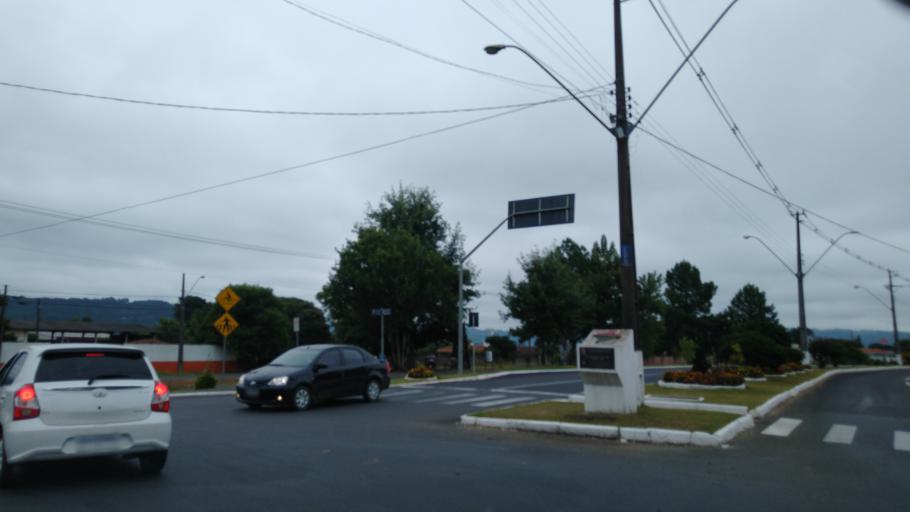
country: BR
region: Santa Catarina
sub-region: Porto Uniao
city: Porto Uniao
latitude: -26.2500
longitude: -51.0840
